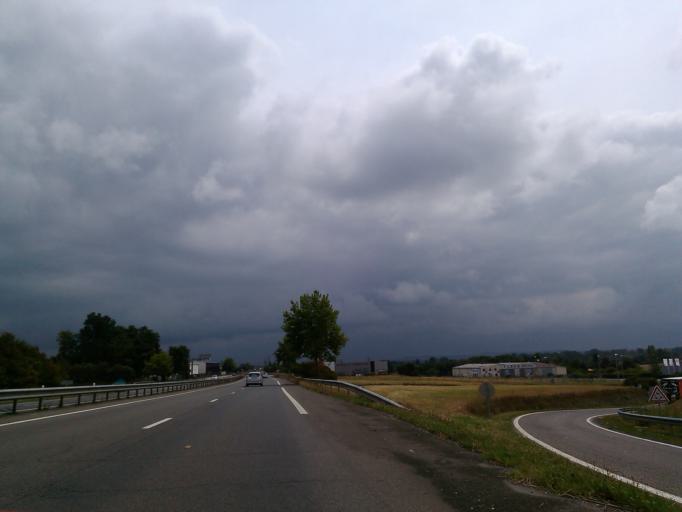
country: FR
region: Poitou-Charentes
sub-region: Departement de la Charente
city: Saint-Brice
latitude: 45.6769
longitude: -0.2767
